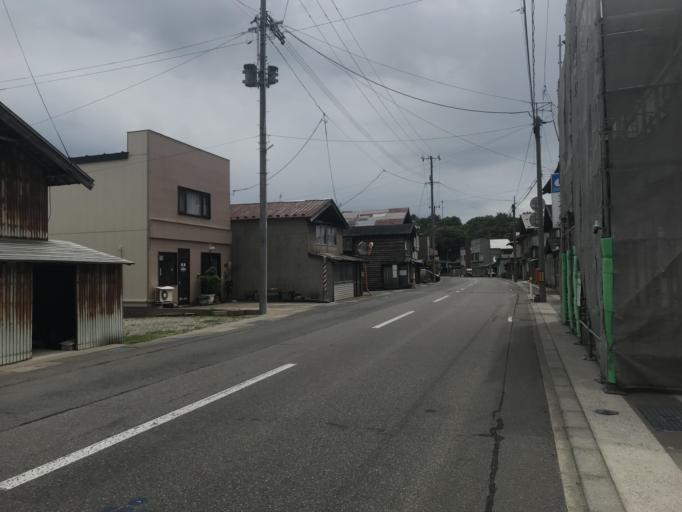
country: JP
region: Aomori
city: Shimokizukuri
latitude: 40.7830
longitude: 140.1988
